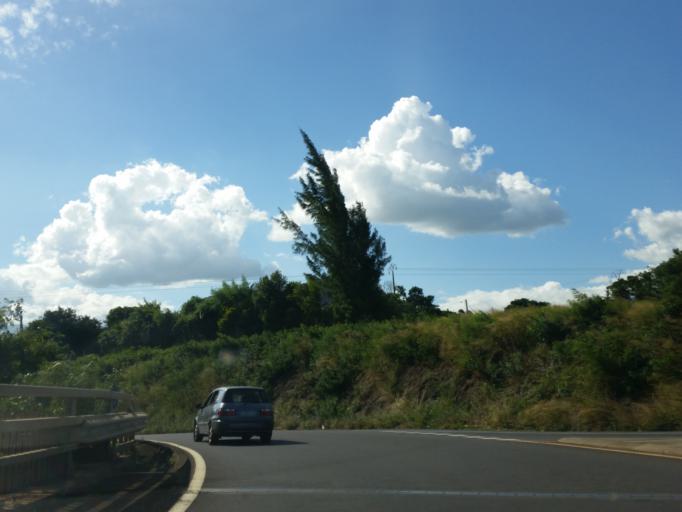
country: RE
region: Reunion
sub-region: Reunion
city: Saint-Pierre
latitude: -21.3357
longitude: 55.4883
